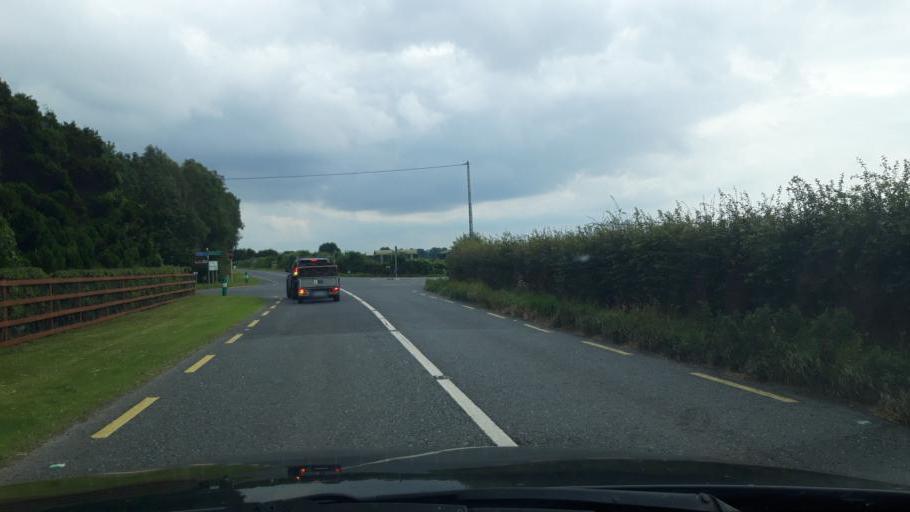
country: IE
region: Leinster
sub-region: Kildare
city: Athy
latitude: 53.0225
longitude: -7.0070
